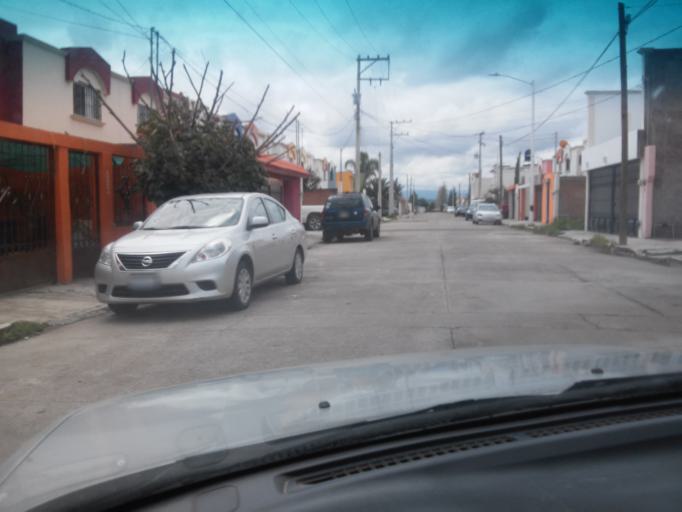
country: MX
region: Durango
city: Victoria de Durango
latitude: 24.0067
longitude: -104.6356
